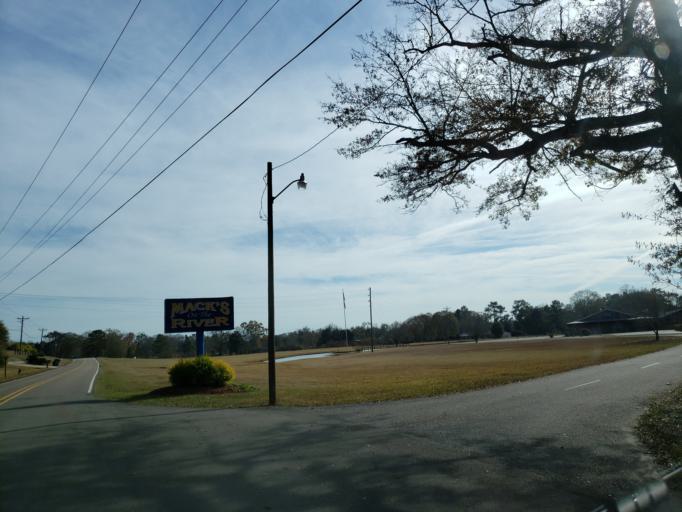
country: US
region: Mississippi
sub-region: Forrest County
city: Rawls Springs
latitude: 31.3968
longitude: -89.3602
